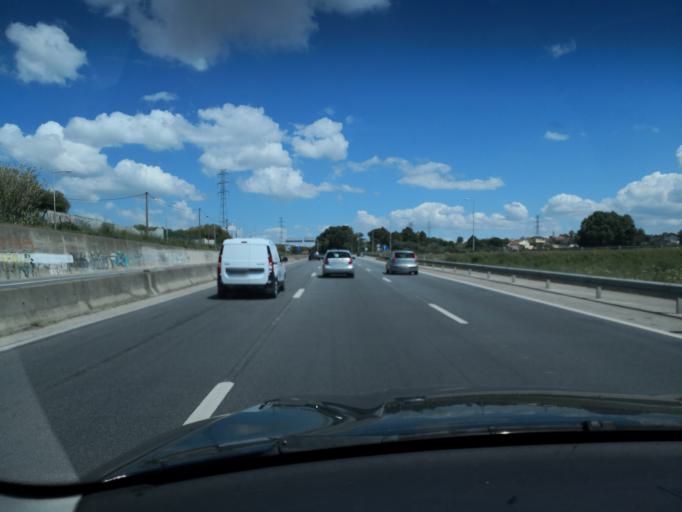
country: PT
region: Setubal
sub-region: Almada
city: Caparica
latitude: 38.6540
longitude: -9.2142
